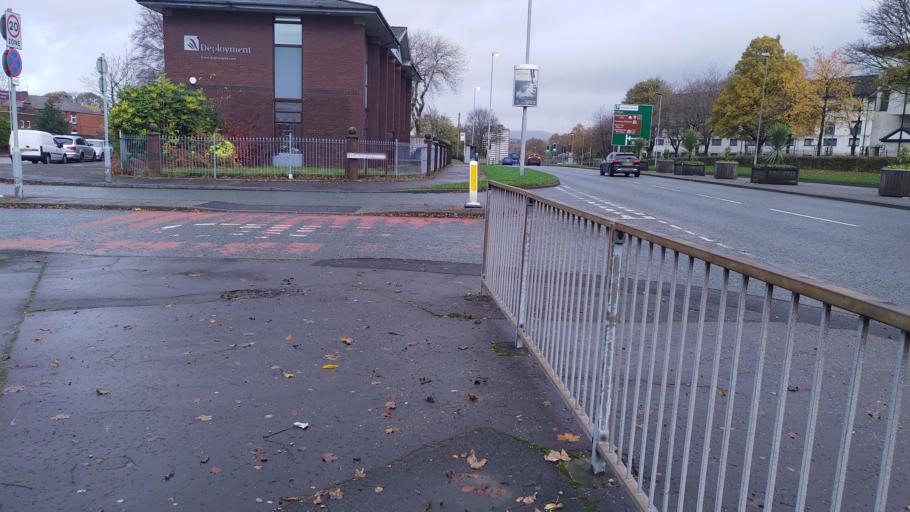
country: GB
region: England
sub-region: Borough of Rochdale
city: Rochdale
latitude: 53.6094
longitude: -2.1645
